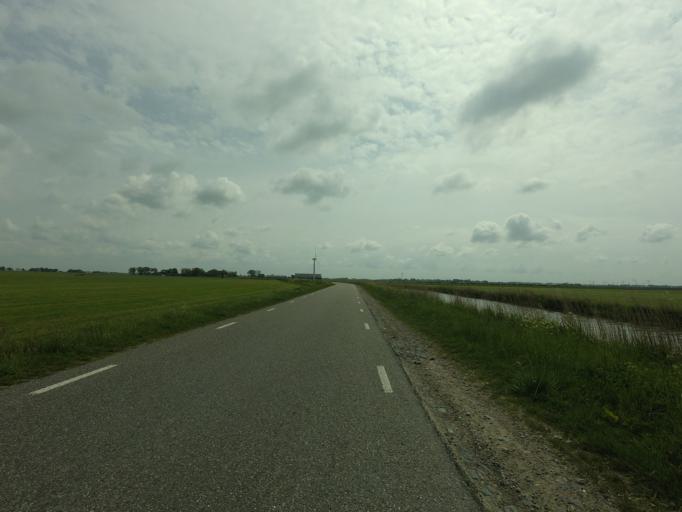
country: NL
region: Friesland
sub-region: Sudwest Fryslan
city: Bolsward
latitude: 53.1024
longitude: 5.5138
